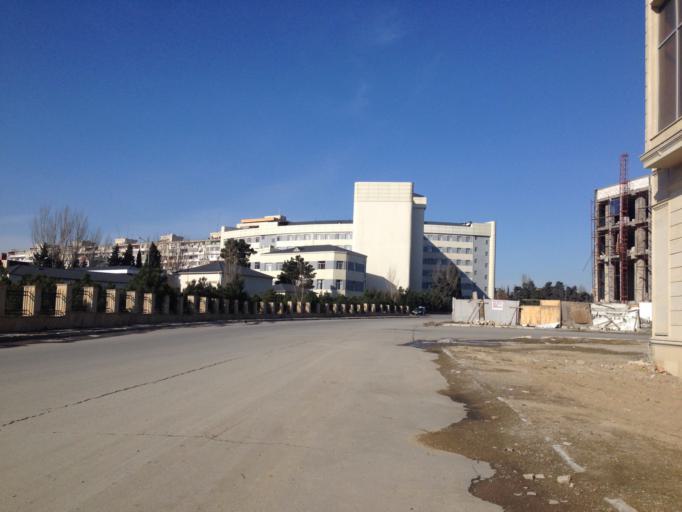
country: AZ
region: Baki
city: Baku
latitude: 40.4120
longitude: 49.8520
